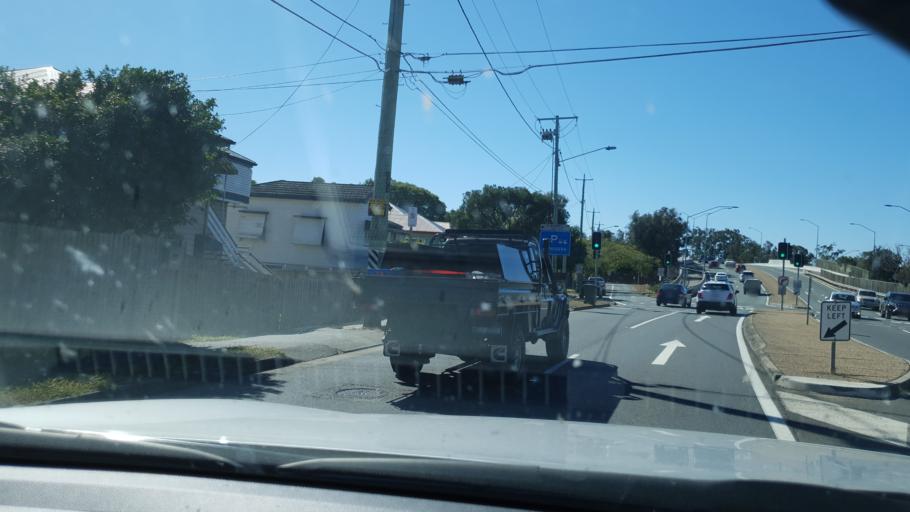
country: AU
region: Queensland
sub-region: Brisbane
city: Everton Park
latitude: -27.4218
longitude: 152.9908
